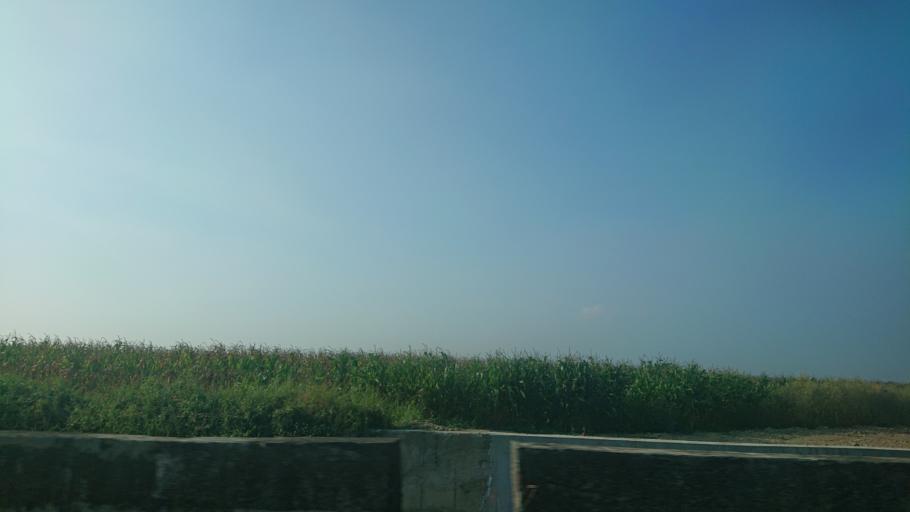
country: TW
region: Taiwan
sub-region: Tainan
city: Tainan
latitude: 23.1383
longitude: 120.2413
